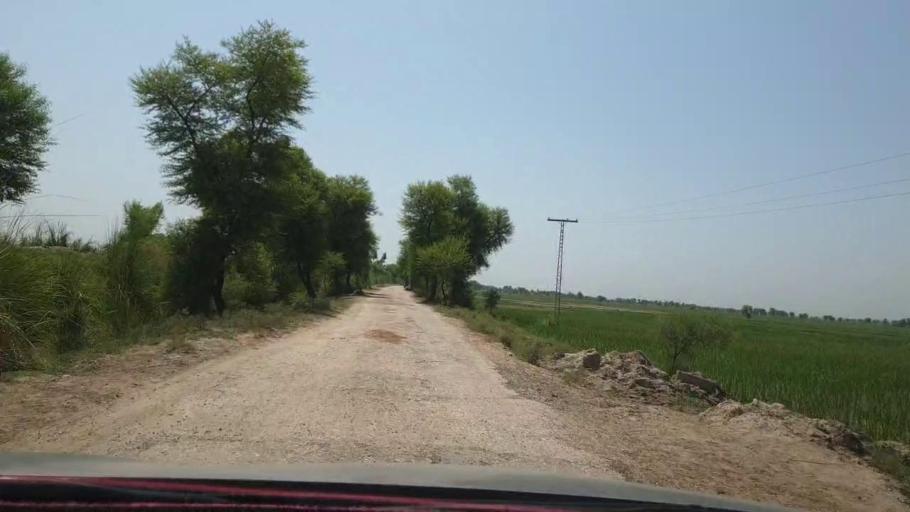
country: PK
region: Sindh
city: Warah
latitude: 27.5057
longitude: 67.7895
